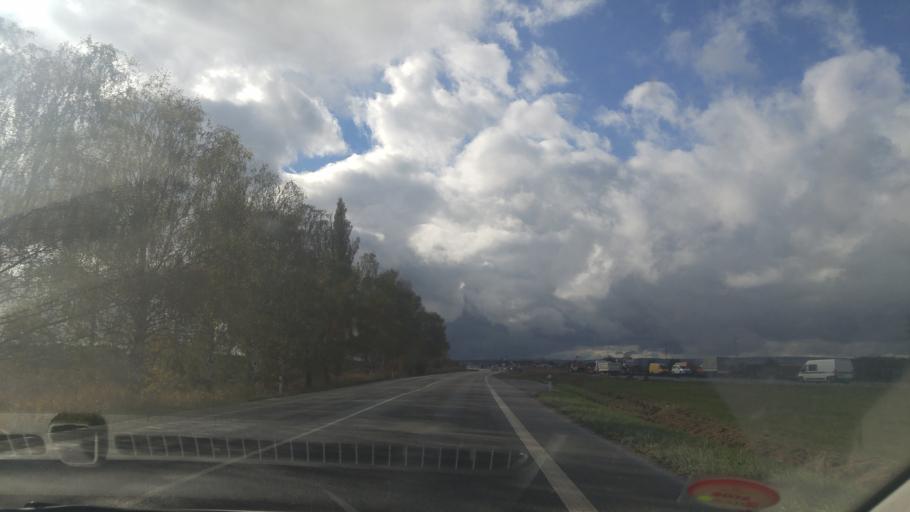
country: CZ
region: Jihocesky
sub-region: Okres Tabor
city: Veseli nad Luznici
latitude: 49.1701
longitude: 14.6736
